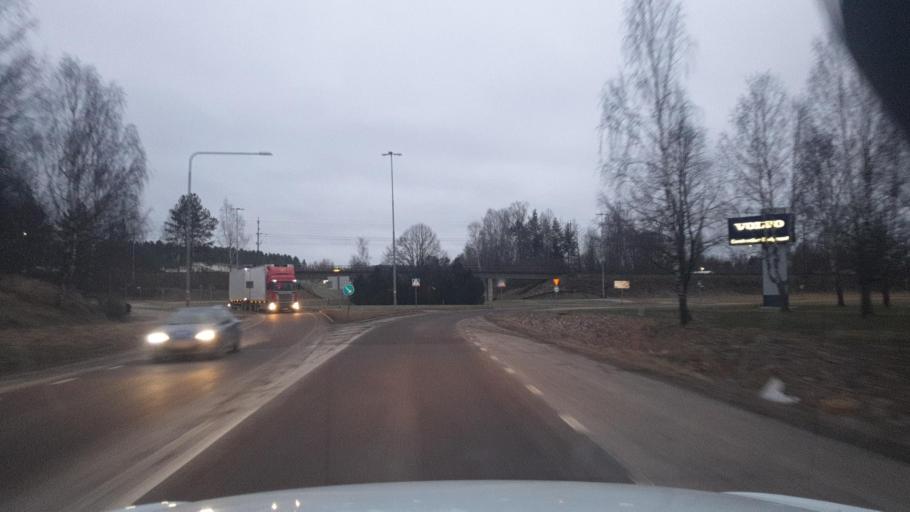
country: SE
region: Vaermland
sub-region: Arvika Kommun
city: Arvika
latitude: 59.6502
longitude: 12.6171
